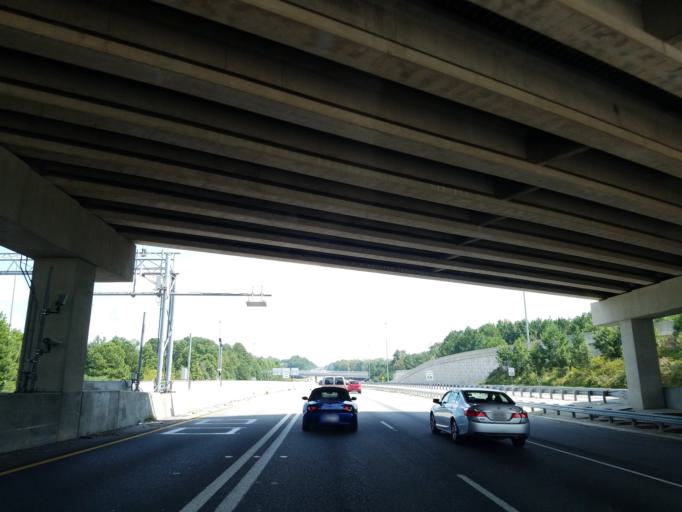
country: US
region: Georgia
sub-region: Gwinnett County
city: Duluth
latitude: 33.9641
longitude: -84.0949
